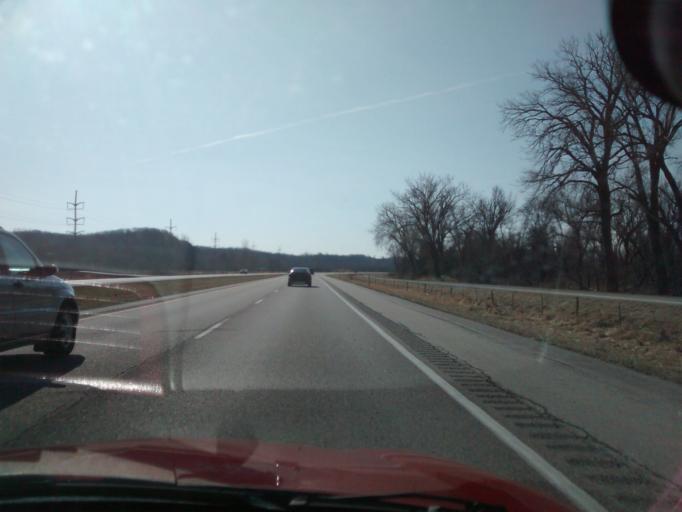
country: US
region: Iowa
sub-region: Pottawattamie County
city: Carter Lake
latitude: 41.3141
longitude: -95.8748
